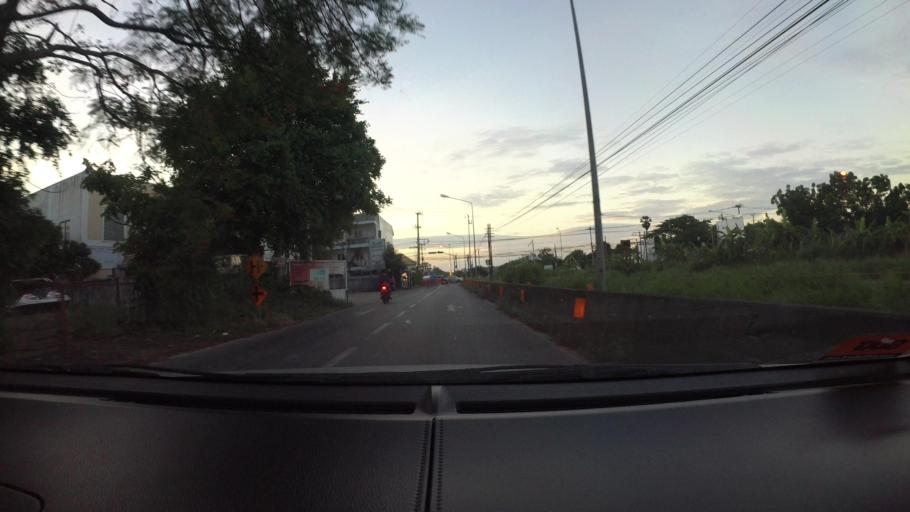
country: TH
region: Chon Buri
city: Phatthaya
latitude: 12.8817
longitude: 100.9045
